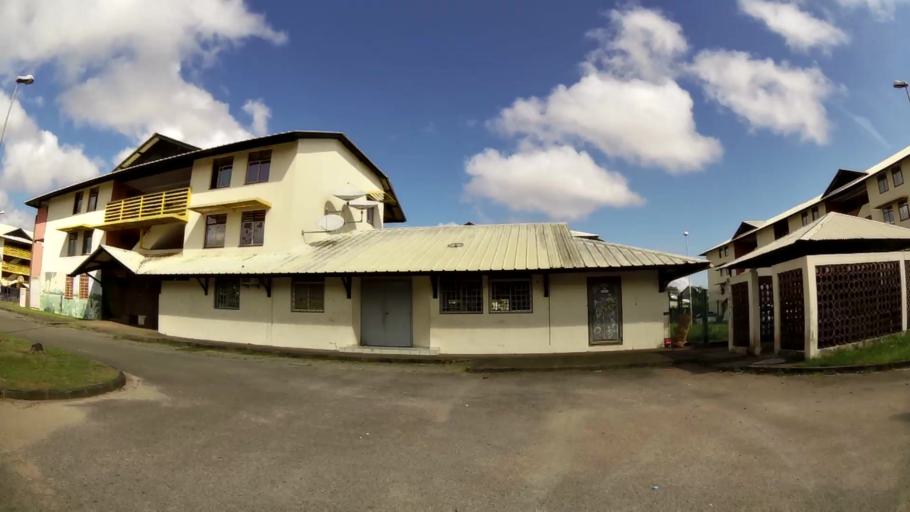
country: GF
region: Guyane
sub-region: Guyane
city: Cayenne
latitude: 4.9356
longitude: -52.3160
